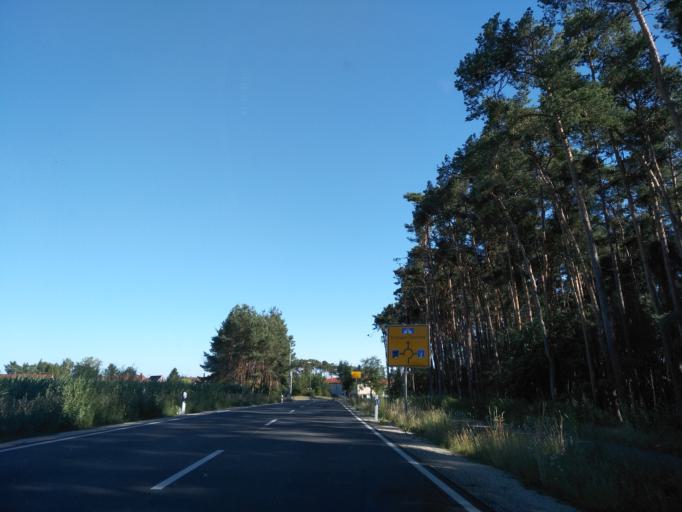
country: DE
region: Bavaria
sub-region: Regierungsbezirk Mittelfranken
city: Hessdorf
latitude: 49.6344
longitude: 10.9315
